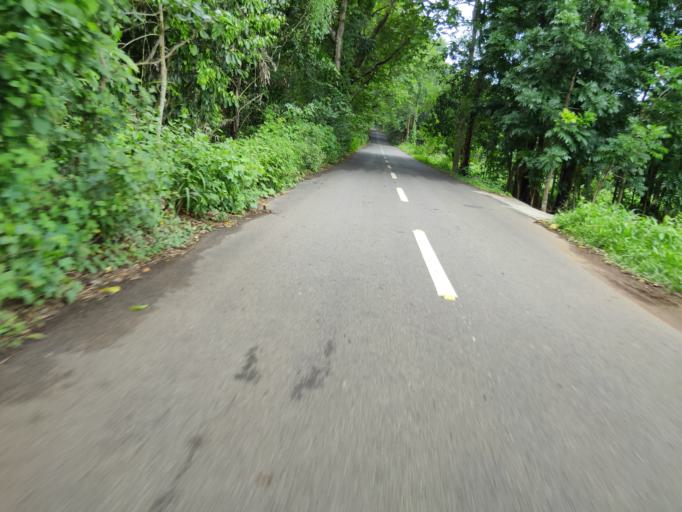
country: IN
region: Kerala
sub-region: Malappuram
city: Manjeri
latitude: 11.2242
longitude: 76.2507
